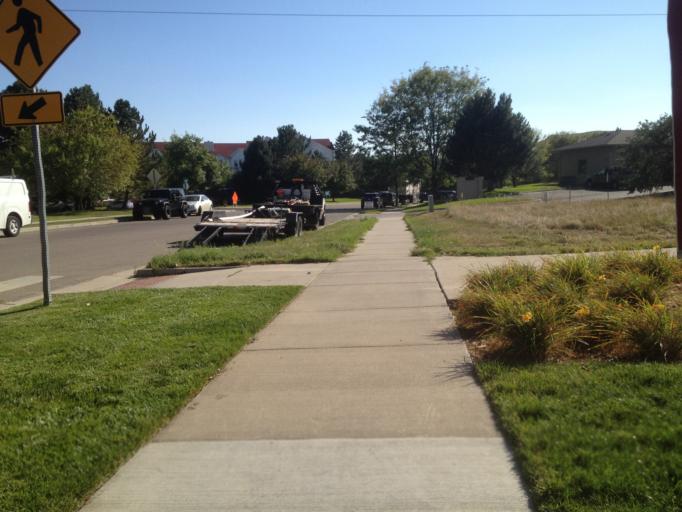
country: US
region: Colorado
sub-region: Boulder County
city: Louisville
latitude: 39.9910
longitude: -105.1243
